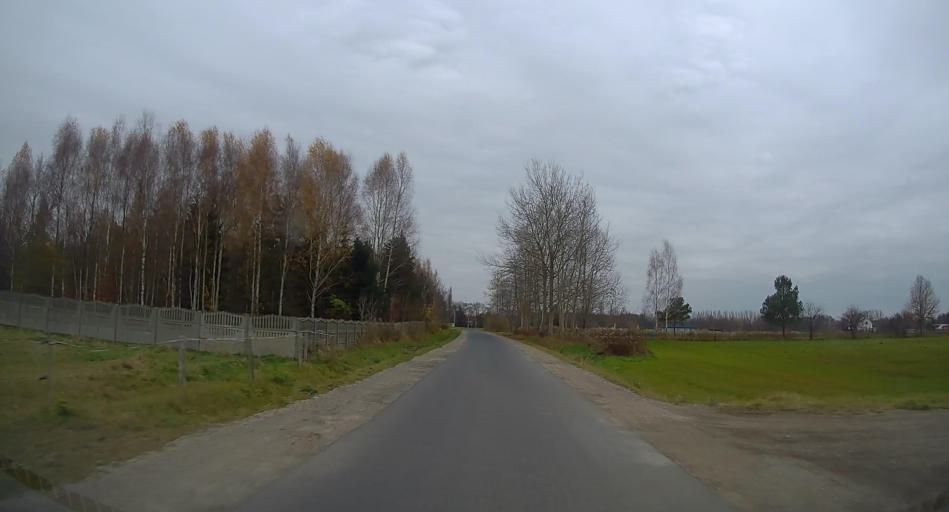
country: PL
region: Lodz Voivodeship
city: Zabia Wola
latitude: 51.9918
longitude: 20.6602
